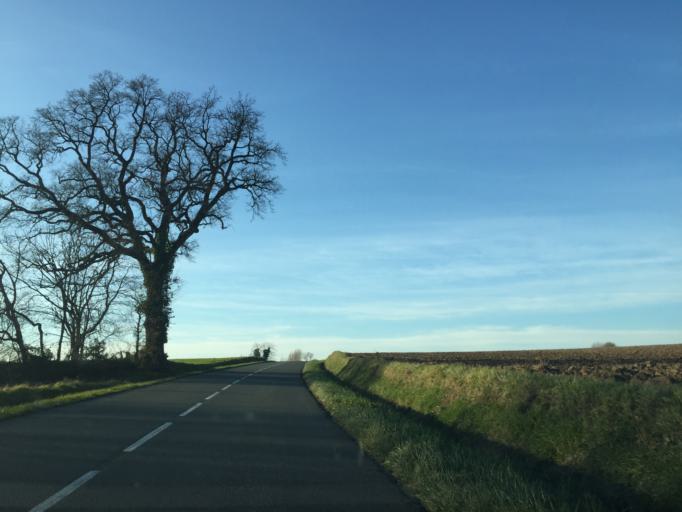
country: FR
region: Aquitaine
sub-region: Departement de la Dordogne
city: Saint-Aulaye
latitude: 45.2790
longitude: 0.1302
